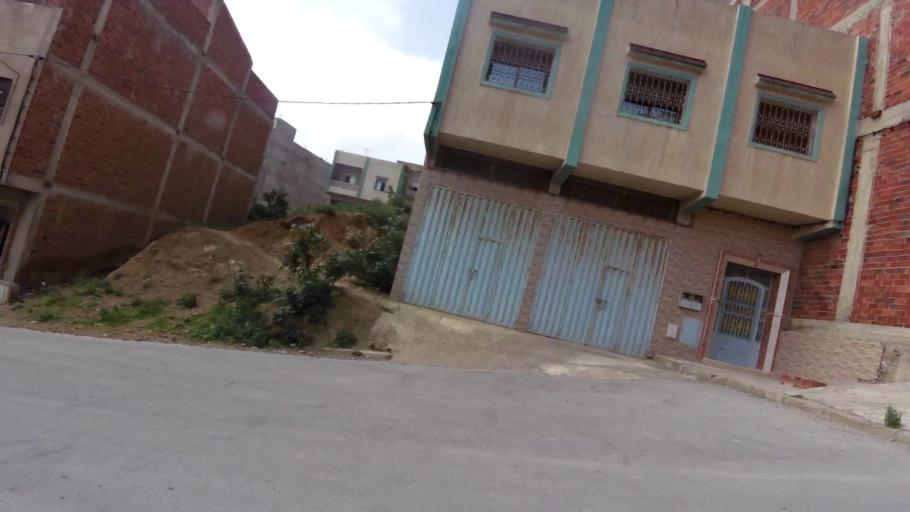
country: MA
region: Tanger-Tetouan
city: Tetouan
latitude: 35.5766
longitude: -5.3921
